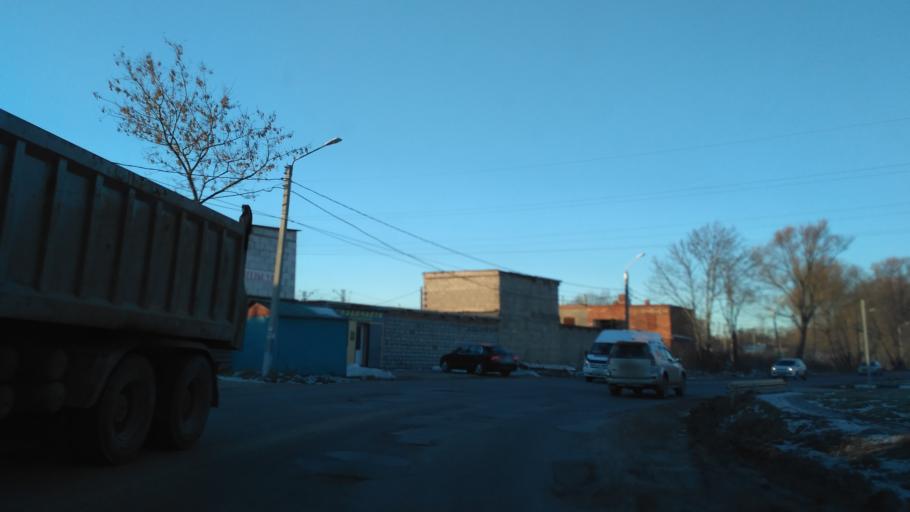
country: RU
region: Tula
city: Tula
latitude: 54.2180
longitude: 37.5930
